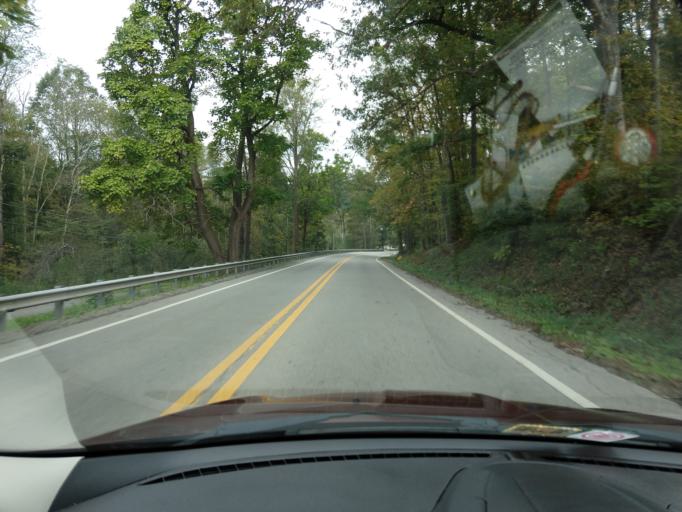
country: US
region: West Virginia
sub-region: Barbour County
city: Belington
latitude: 39.0212
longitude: -79.9375
